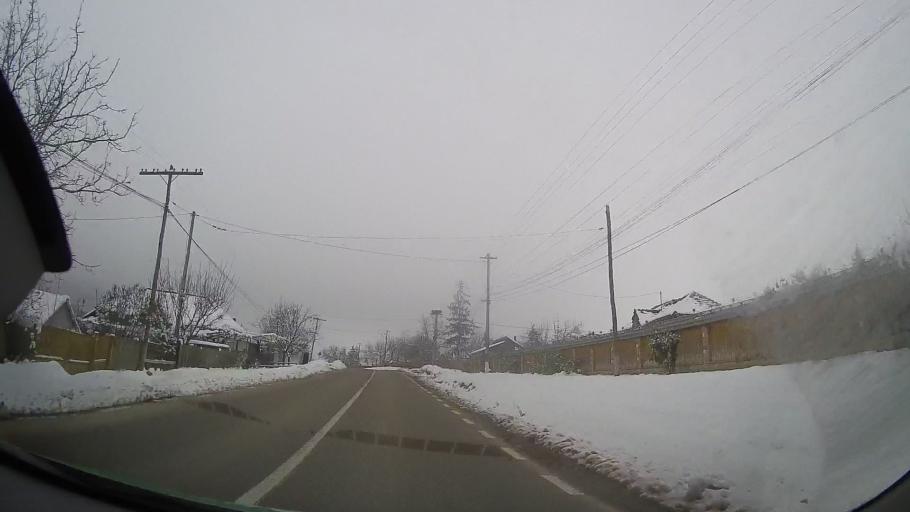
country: RO
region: Vaslui
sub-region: Comuna Todiresti
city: Todiresti
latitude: 46.8418
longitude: 27.3703
